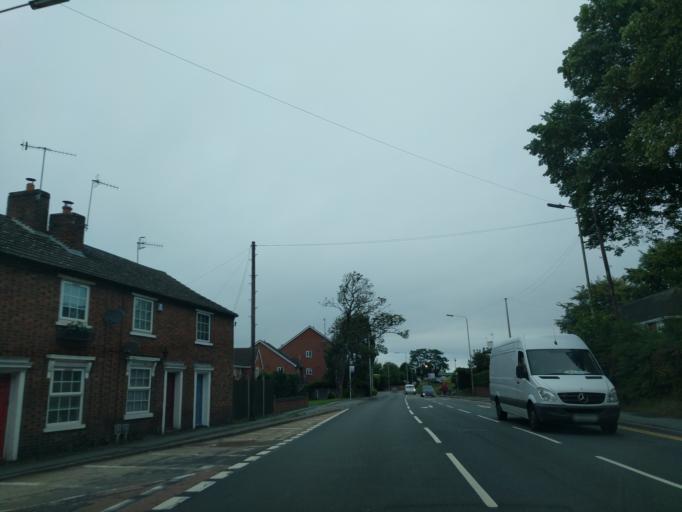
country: GB
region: England
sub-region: Dudley
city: Stourbridge
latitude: 52.4445
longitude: -2.1388
